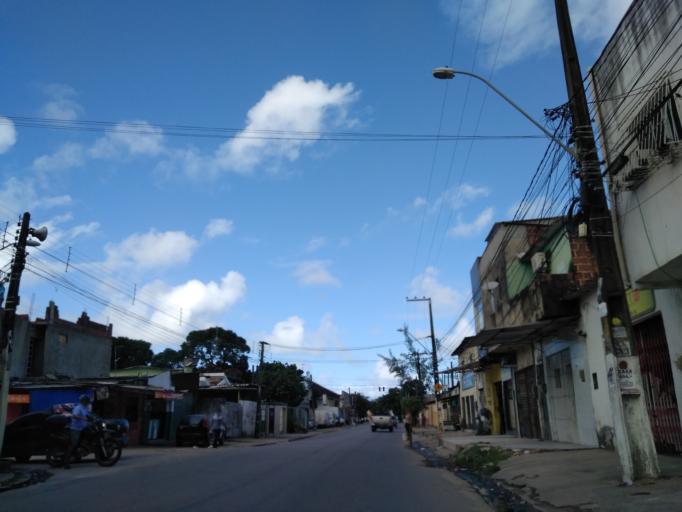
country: BR
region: Pernambuco
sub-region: Recife
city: Recife
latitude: -8.0760
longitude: -34.9146
